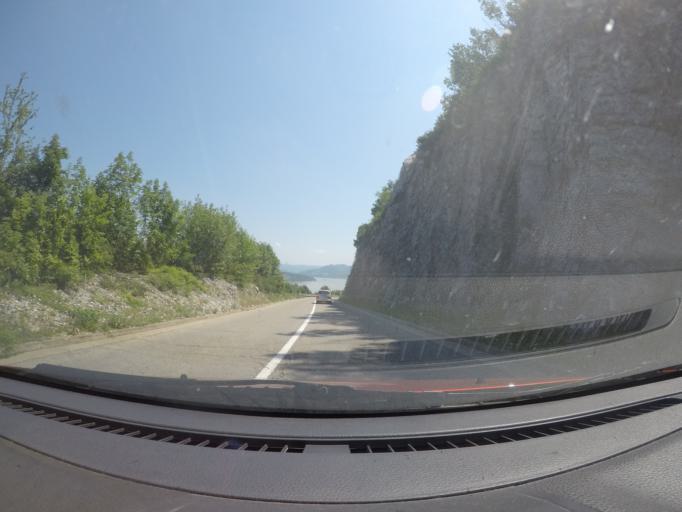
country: RO
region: Mehedinti
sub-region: Comuna Eselnita
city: Eselnita
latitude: 44.6652
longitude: 22.3407
